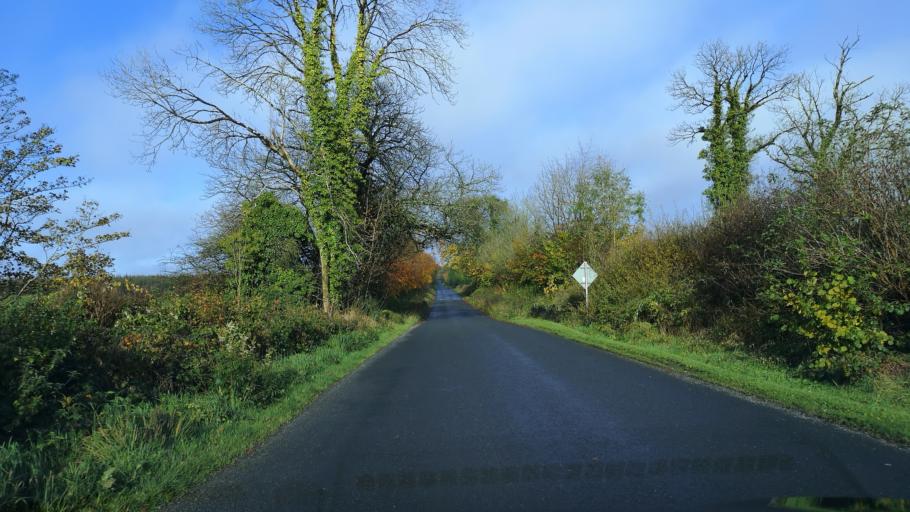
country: IE
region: Leinster
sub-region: An Iarmhi
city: Moate
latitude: 53.3820
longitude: -7.8027
